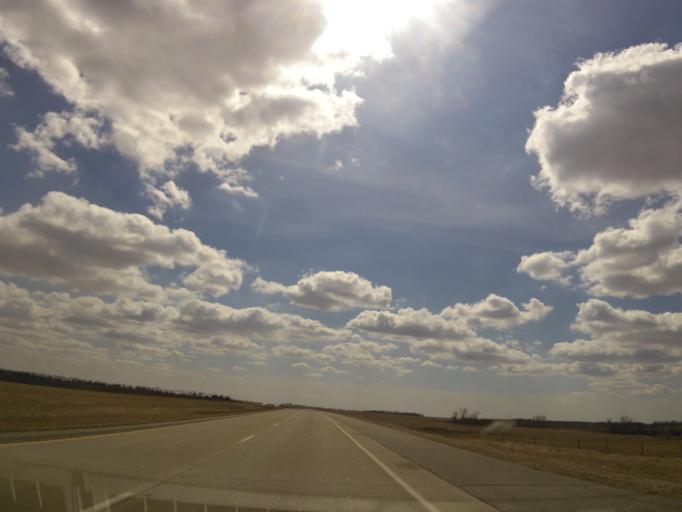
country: US
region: South Dakota
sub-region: Codington County
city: Watertown
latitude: 45.1926
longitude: -97.0567
